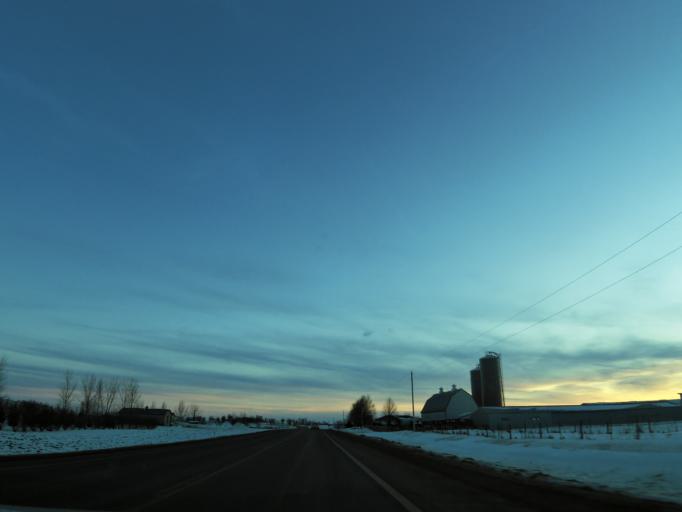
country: US
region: Minnesota
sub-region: Carver County
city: Chaska
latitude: 44.7436
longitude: -93.5619
